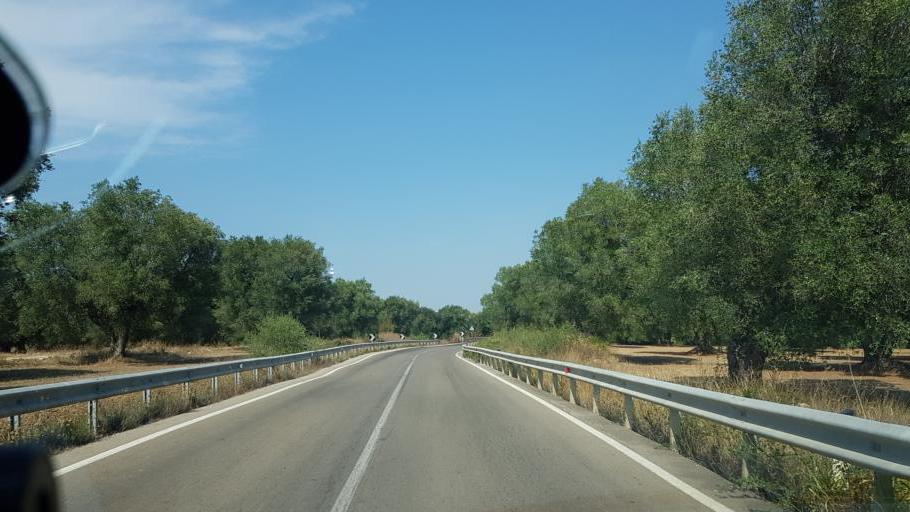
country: IT
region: Apulia
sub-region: Provincia di Brindisi
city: Torre Santa Susanna
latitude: 40.4966
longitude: 17.7169
